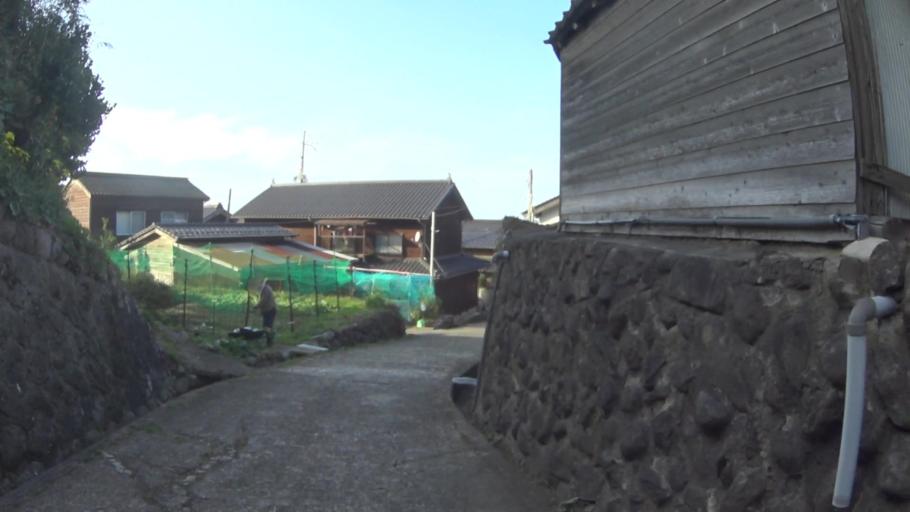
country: JP
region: Kyoto
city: Miyazu
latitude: 35.7630
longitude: 135.2061
